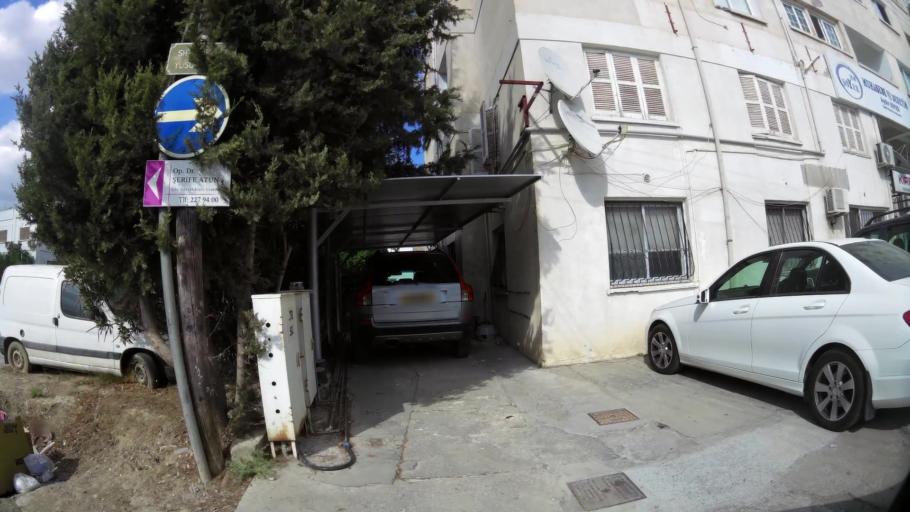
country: CY
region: Lefkosia
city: Nicosia
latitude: 35.1852
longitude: 33.3570
